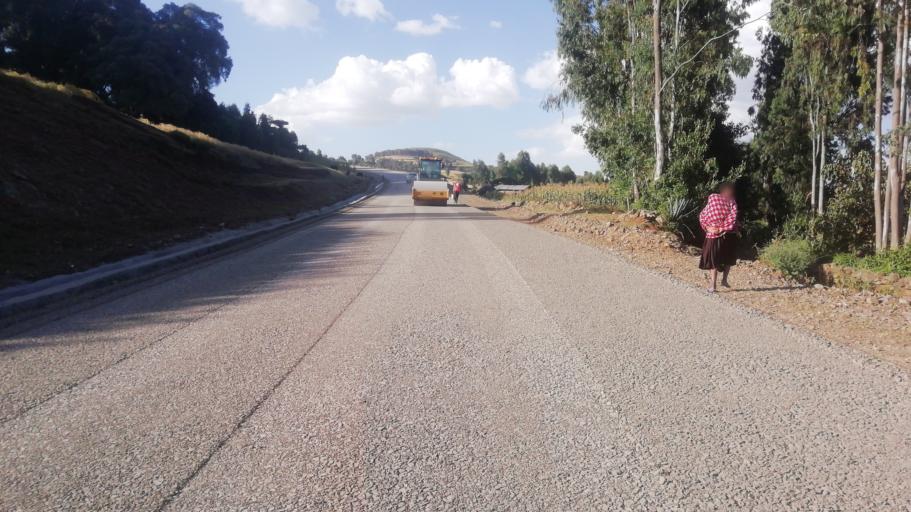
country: ET
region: Amhara
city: Addiet Canna
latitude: 11.3467
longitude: 37.8759
